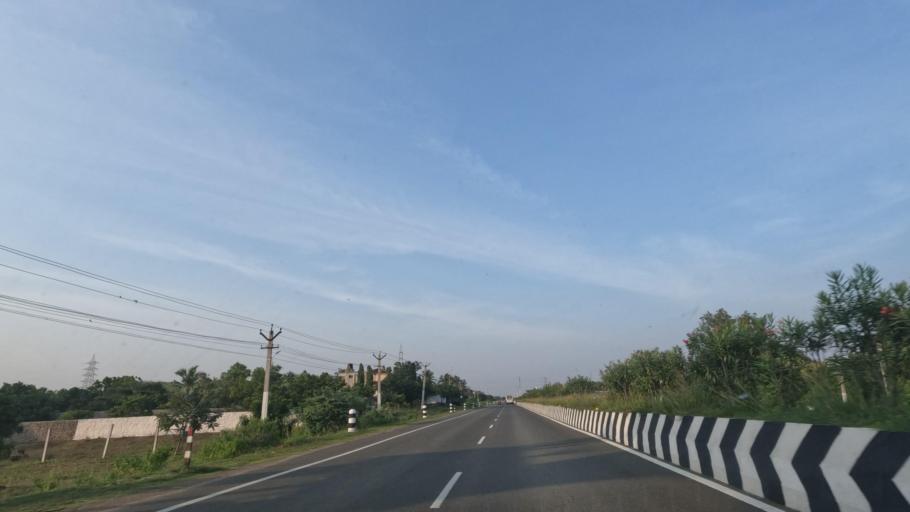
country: IN
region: Tamil Nadu
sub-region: Kancheepuram
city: Mamallapuram
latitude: 12.6991
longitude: 80.2213
